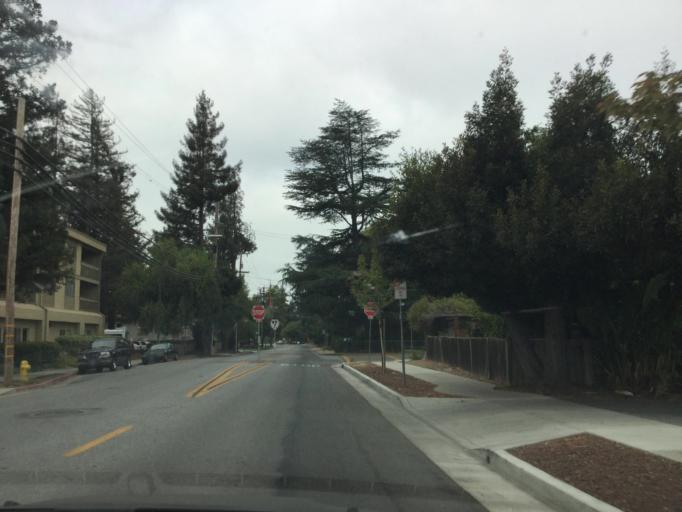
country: US
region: California
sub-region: Santa Clara County
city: Campbell
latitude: 37.2807
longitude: -121.9536
